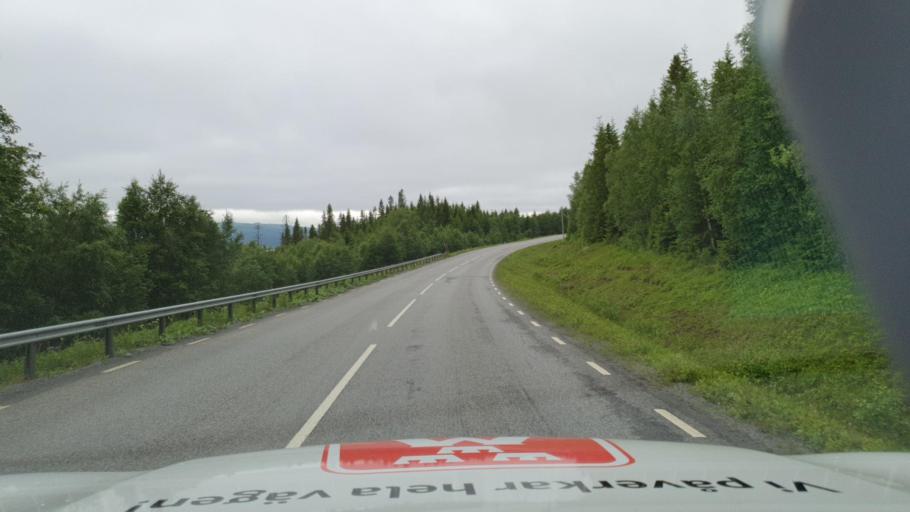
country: SE
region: Jaemtland
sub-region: Are Kommun
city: Are
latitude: 63.5355
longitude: 13.0606
